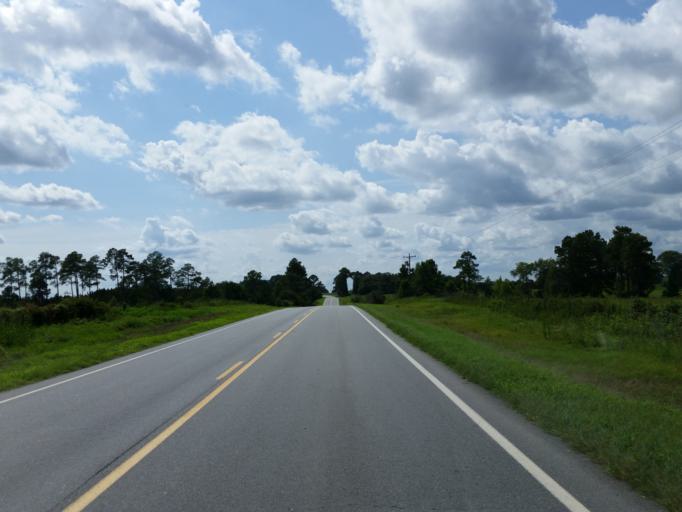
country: US
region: Georgia
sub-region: Turner County
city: Ashburn
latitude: 31.6549
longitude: -83.5552
